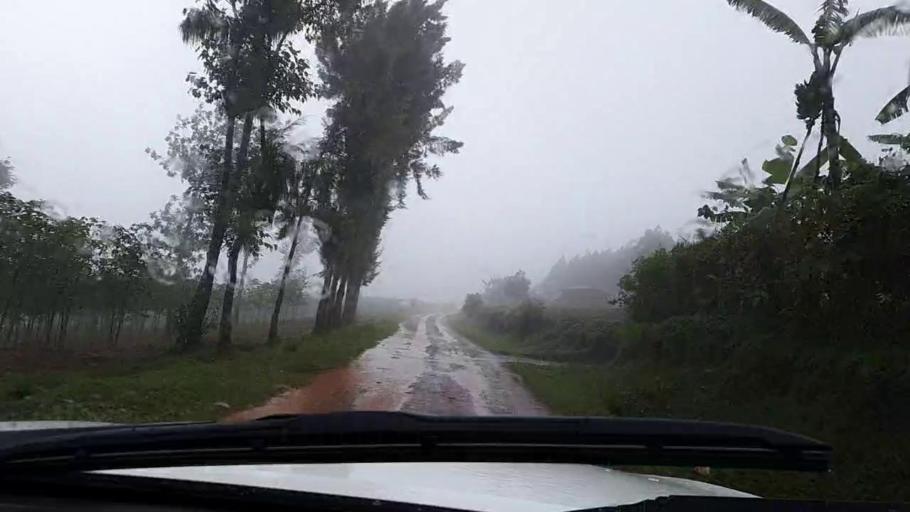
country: RW
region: Northern Province
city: Byumba
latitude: -1.7341
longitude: 30.0130
